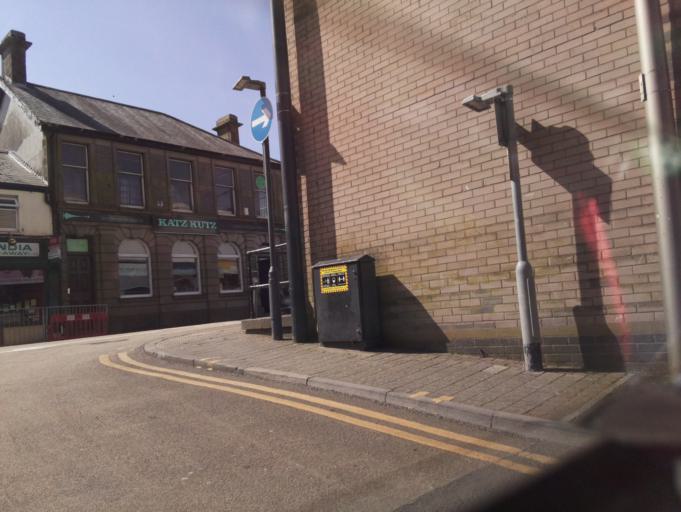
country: GB
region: Wales
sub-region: Rhondda Cynon Taf
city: Mountain Ash
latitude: 51.6823
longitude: -3.3786
